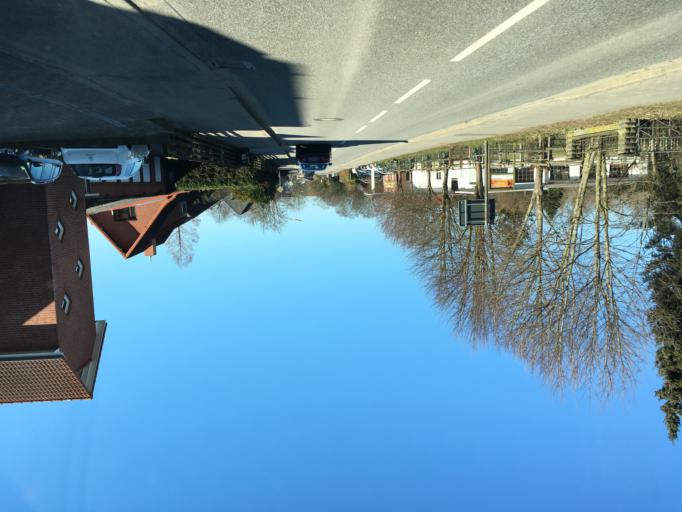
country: DE
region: Schleswig-Holstein
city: Berkenthin
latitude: 53.7346
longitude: 10.6393
